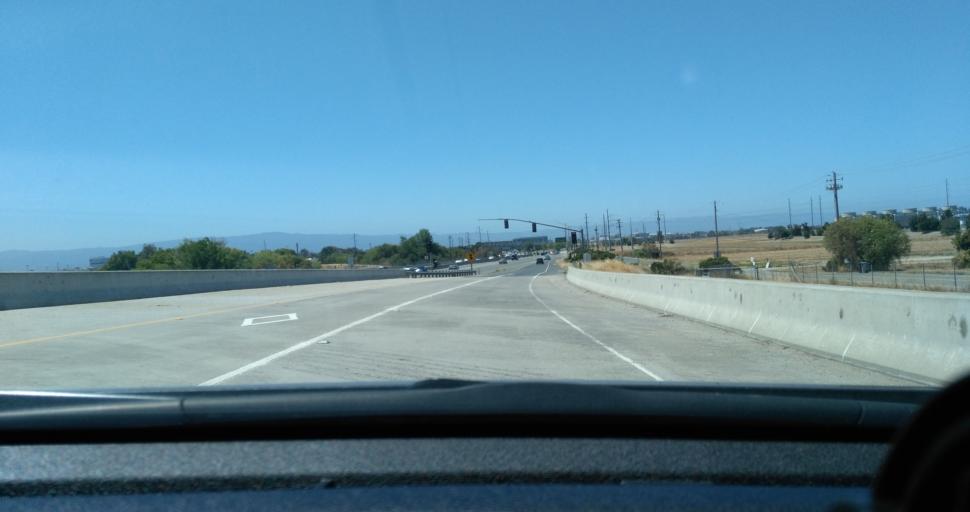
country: US
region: California
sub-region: Santa Clara County
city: Milpitas
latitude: 37.4232
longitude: -121.9259
